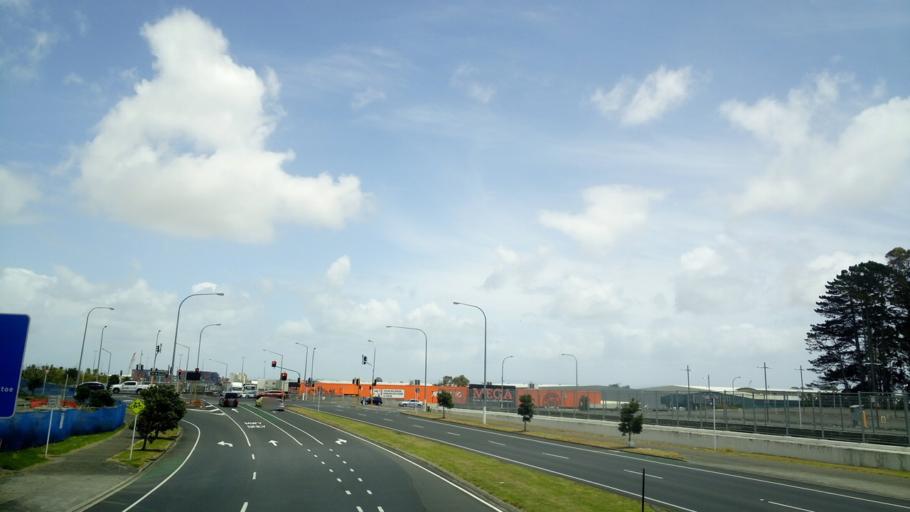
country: NZ
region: Auckland
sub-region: Auckland
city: Manukau City
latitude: -36.9949
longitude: 174.8757
